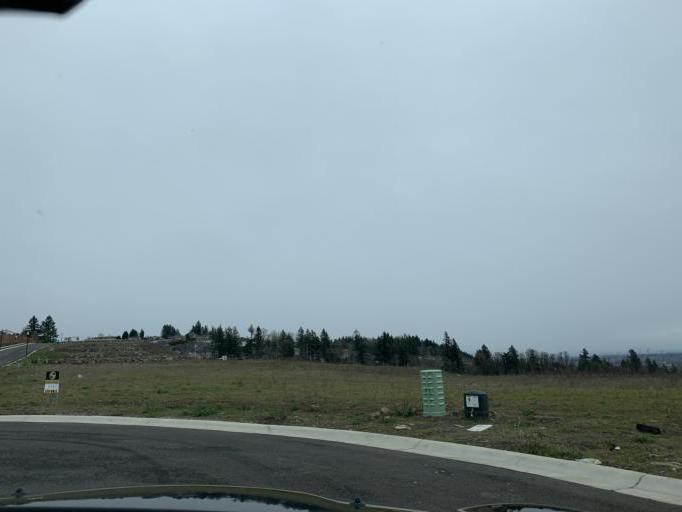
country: US
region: Washington
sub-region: Clark County
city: Mill Plain
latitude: 45.5903
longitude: -122.4724
